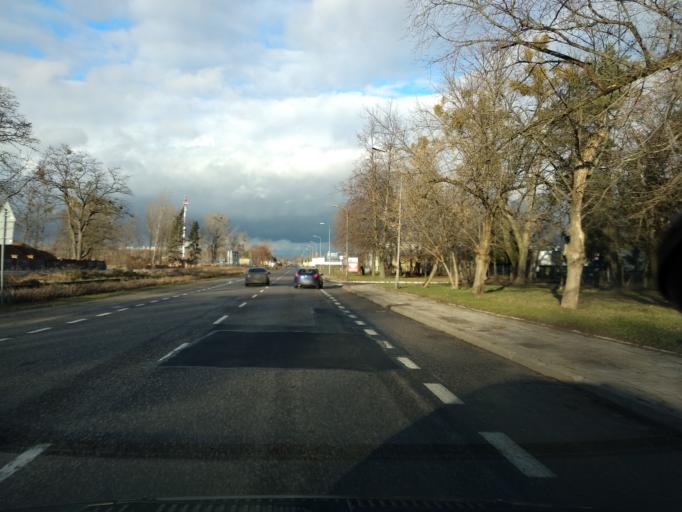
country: PL
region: Greater Poland Voivodeship
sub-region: Konin
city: Konin
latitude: 52.2459
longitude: 18.2702
